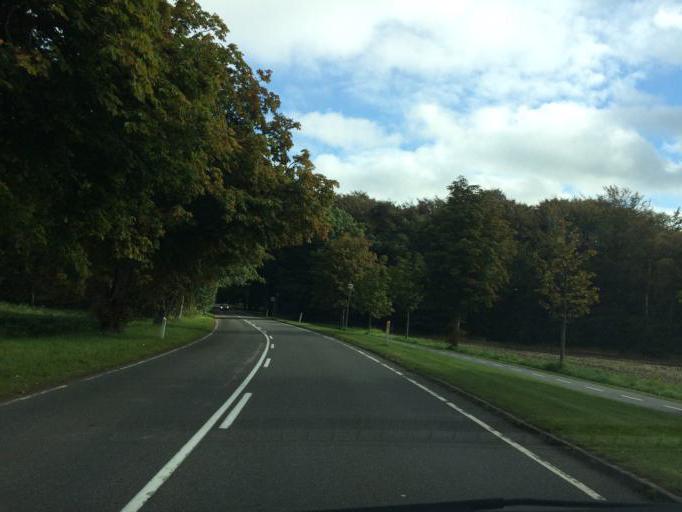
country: DK
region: North Denmark
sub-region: Bronderslev Kommune
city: Dronninglund
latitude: 57.1543
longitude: 10.2701
